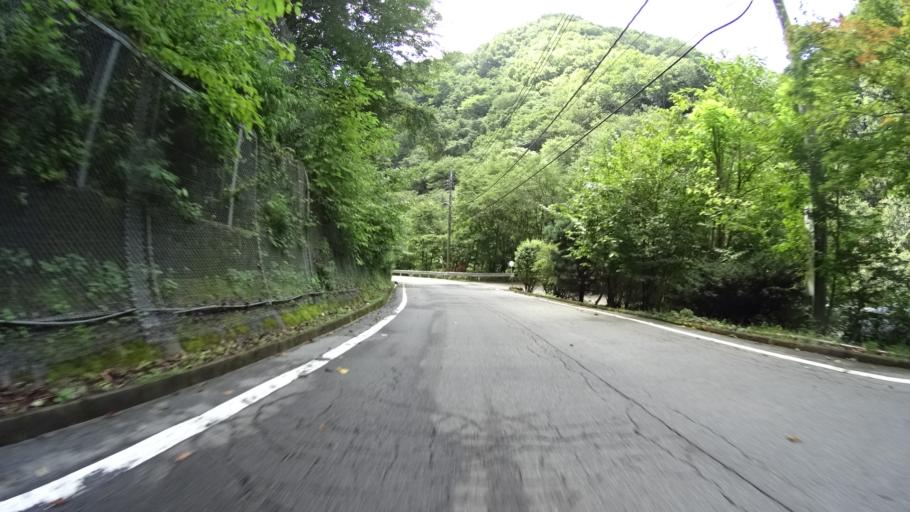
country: JP
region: Yamanashi
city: Enzan
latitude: 35.6746
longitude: 138.8067
